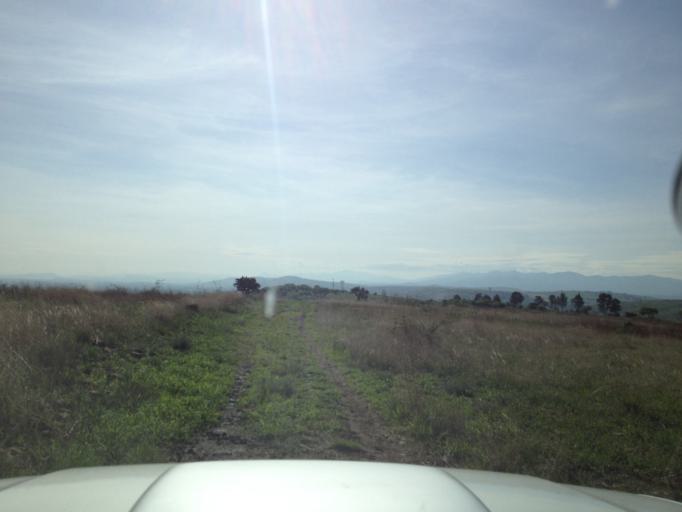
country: MX
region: Michoacan
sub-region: Tarimbaro
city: El Colegio
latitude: 19.7692
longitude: -101.1813
